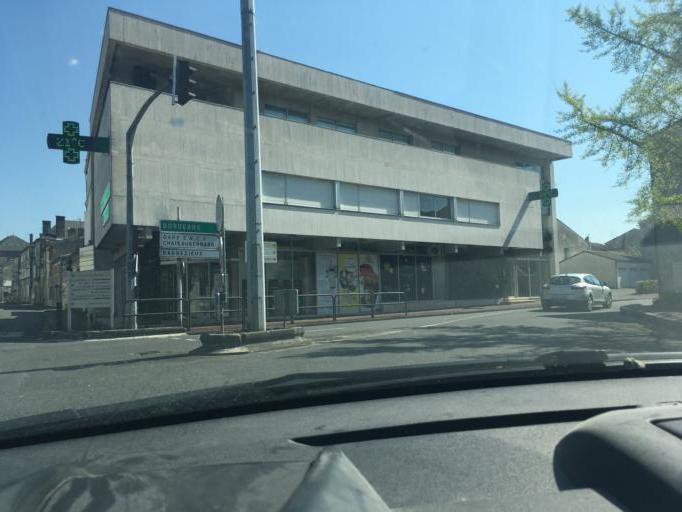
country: FR
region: Poitou-Charentes
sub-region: Departement de la Charente
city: Cognac
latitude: 45.6879
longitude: -0.3345
